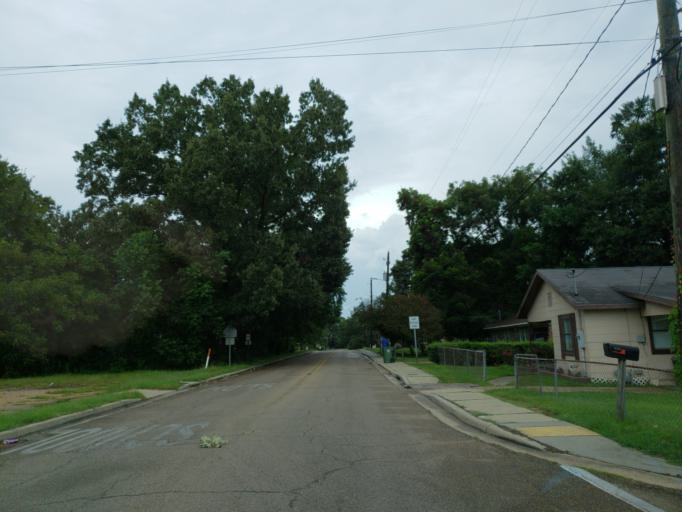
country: US
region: Mississippi
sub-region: Forrest County
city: Hattiesburg
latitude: 31.3108
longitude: -89.2994
